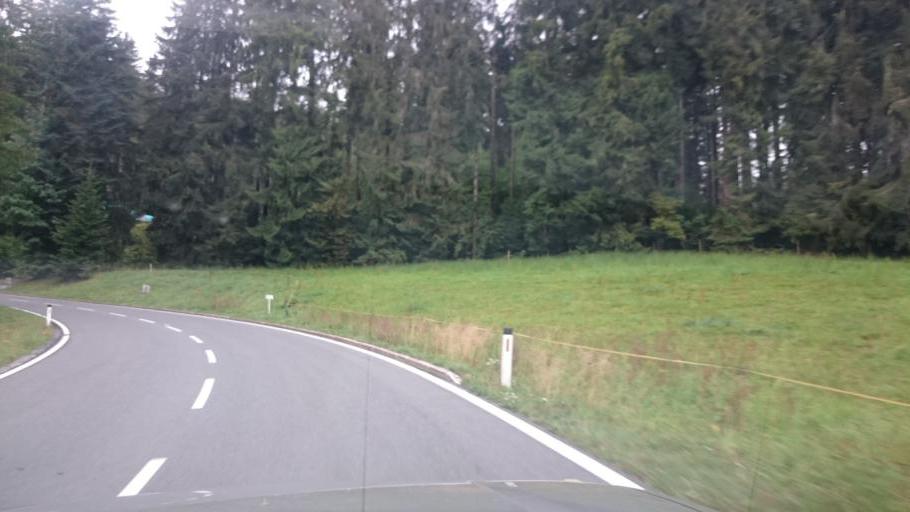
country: AT
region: Vorarlberg
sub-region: Politischer Bezirk Bregenz
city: Bildstein
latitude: 47.4278
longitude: 9.7907
